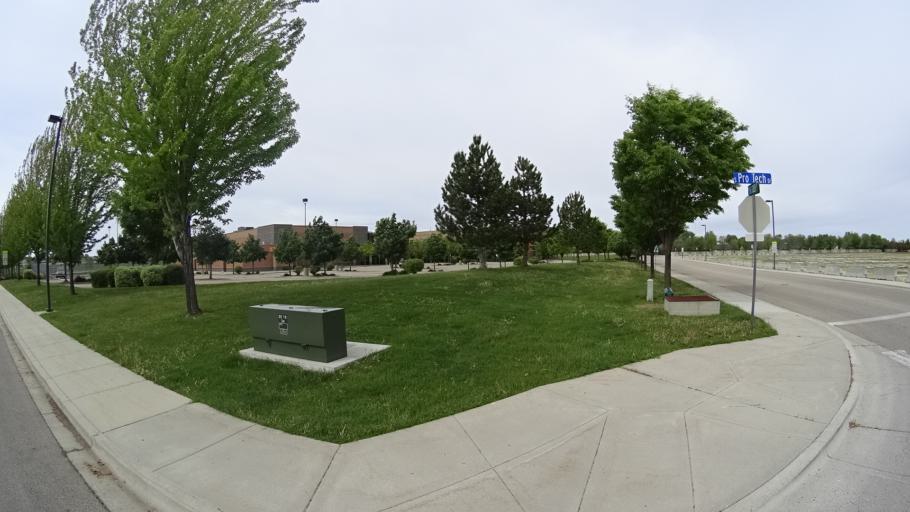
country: US
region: Idaho
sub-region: Ada County
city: Garden City
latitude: 43.5718
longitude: -116.2841
